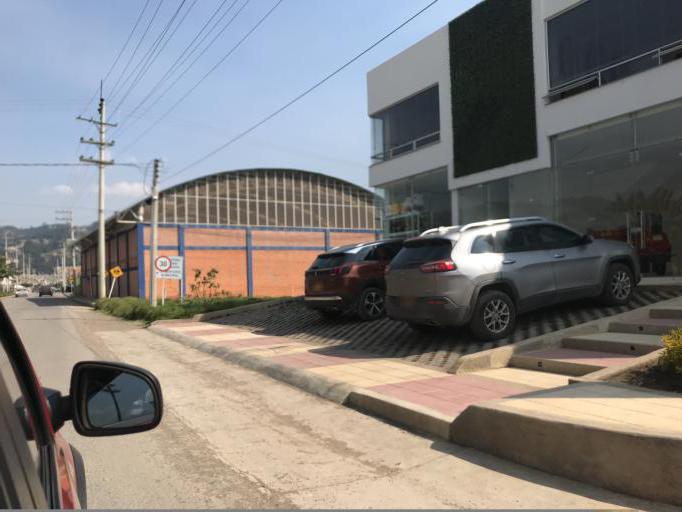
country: CO
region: Boyaca
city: Samaca
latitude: 5.4975
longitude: -73.4892
